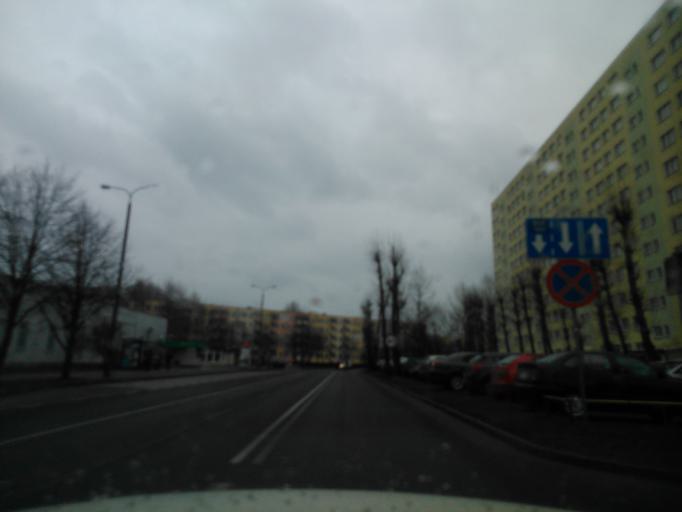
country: PL
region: Kujawsko-Pomorskie
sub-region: Torun
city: Torun
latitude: 53.0293
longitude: 18.6526
